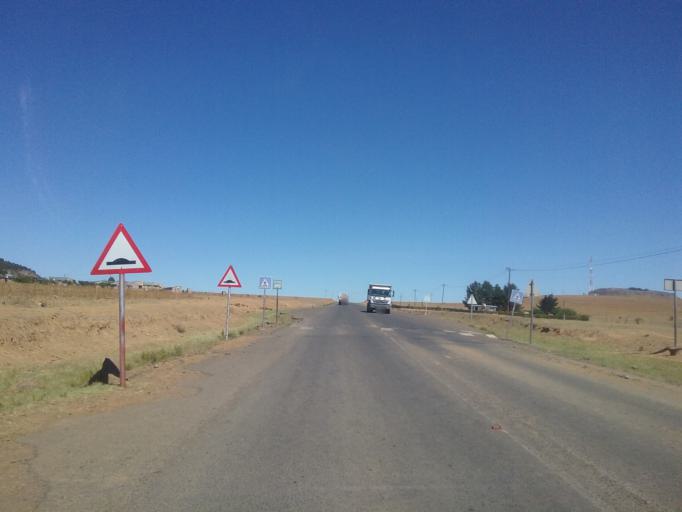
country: LS
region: Quthing
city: Quthing
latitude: -30.3943
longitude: 27.6372
